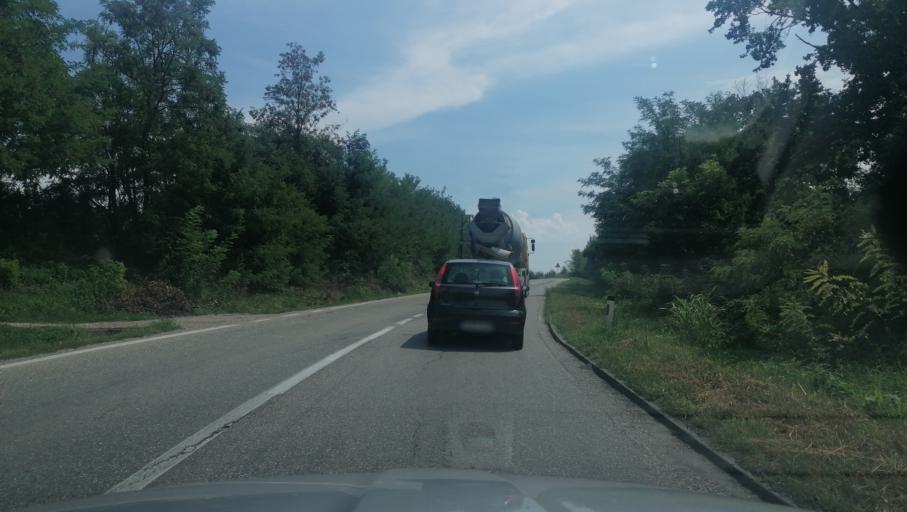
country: BA
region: Republika Srpska
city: Velika Obarska
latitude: 44.7823
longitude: 19.0981
